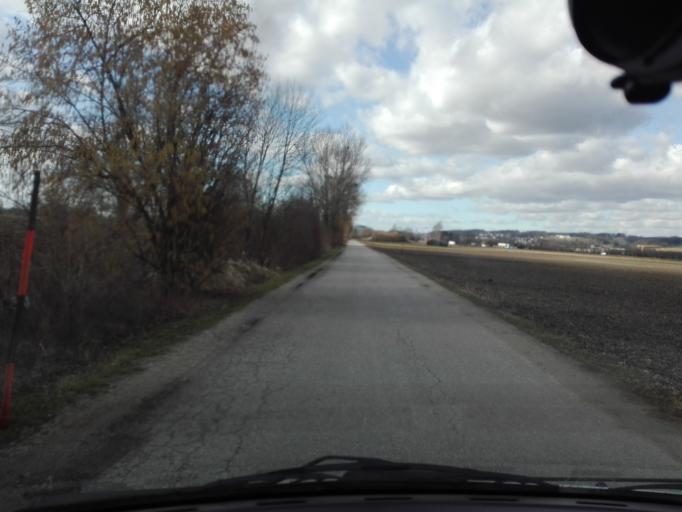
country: AT
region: Upper Austria
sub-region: Politischer Bezirk Perg
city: Perg
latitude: 48.2293
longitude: 14.6518
